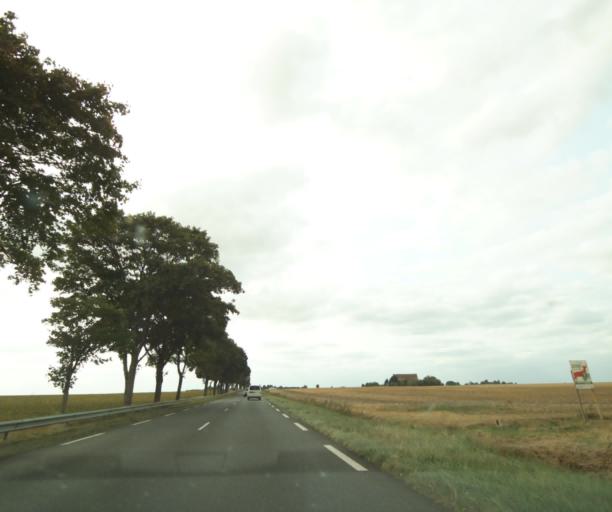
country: FR
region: Centre
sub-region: Departement d'Indre-et-Loire
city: Reignac-sur-Indre
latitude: 47.1916
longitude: 0.9301
